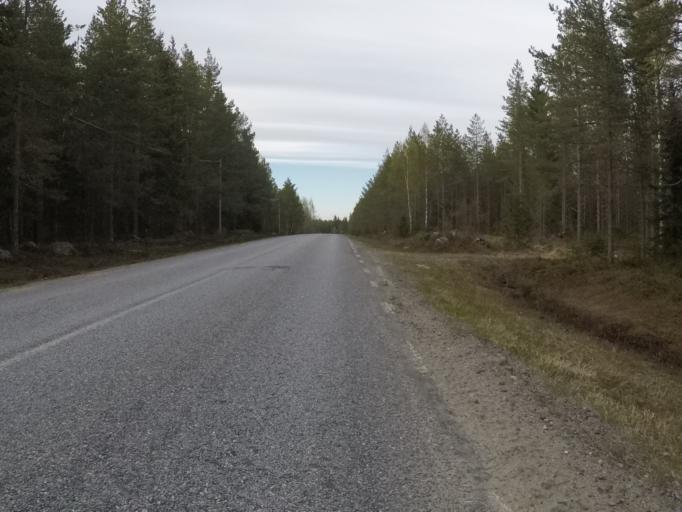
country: SE
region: Vaesterbotten
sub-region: Umea Kommun
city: Saevar
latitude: 63.9265
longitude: 20.7746
